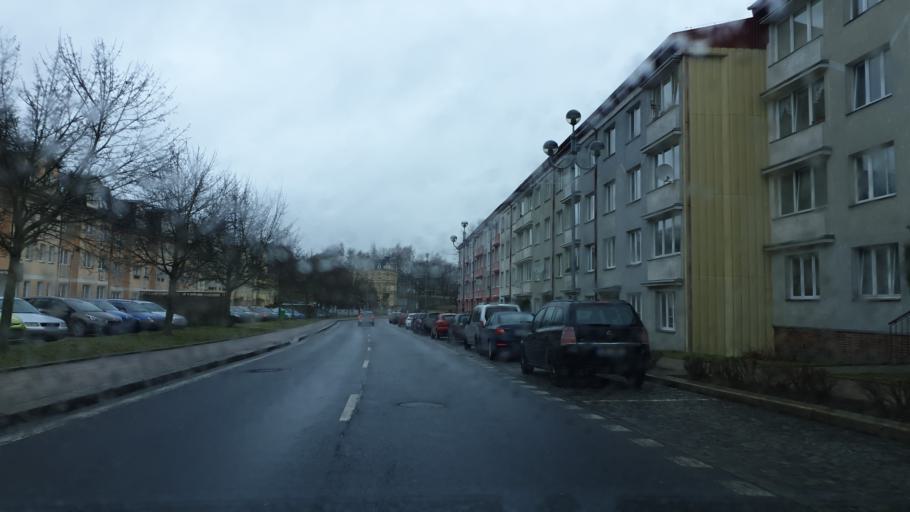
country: CZ
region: Karlovarsky
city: As
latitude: 50.2232
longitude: 12.1868
